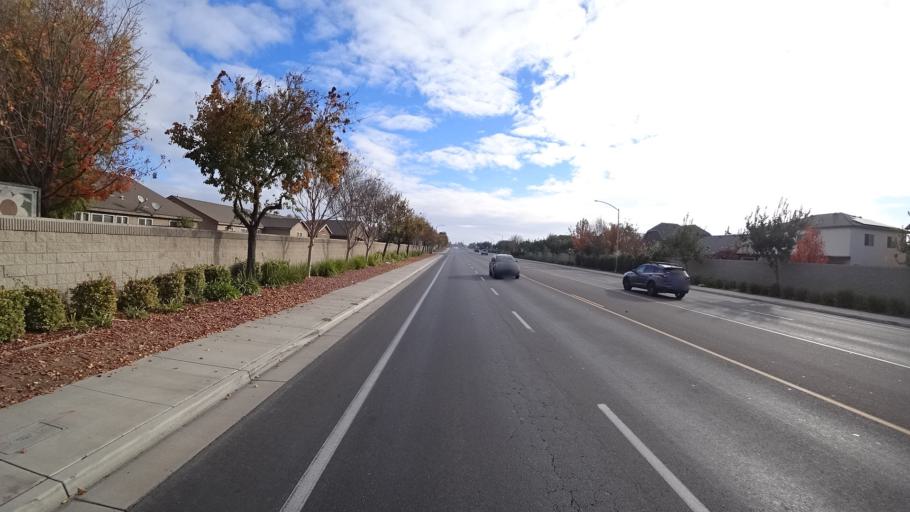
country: US
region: California
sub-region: Kern County
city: Greenacres
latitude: 35.3035
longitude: -119.1046
